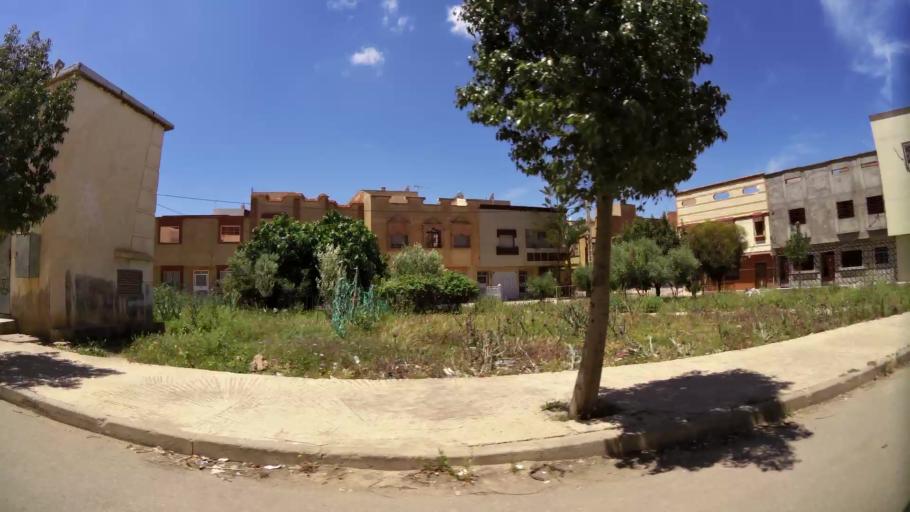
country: MA
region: Oriental
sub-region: Oujda-Angad
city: Oujda
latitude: 34.6643
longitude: -1.9402
